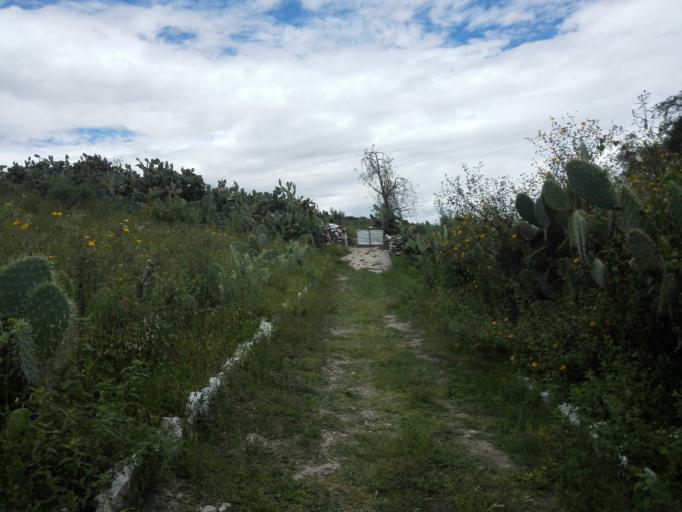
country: PE
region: Ayacucho
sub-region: Provincia de Huamanga
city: Pacaycasa
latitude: -13.0641
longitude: -74.1948
